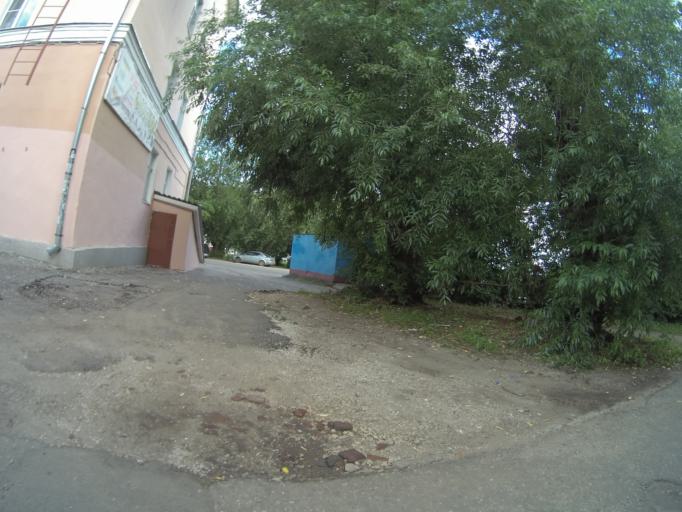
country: RU
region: Vladimir
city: Vladimir
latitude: 56.1214
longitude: 40.3830
